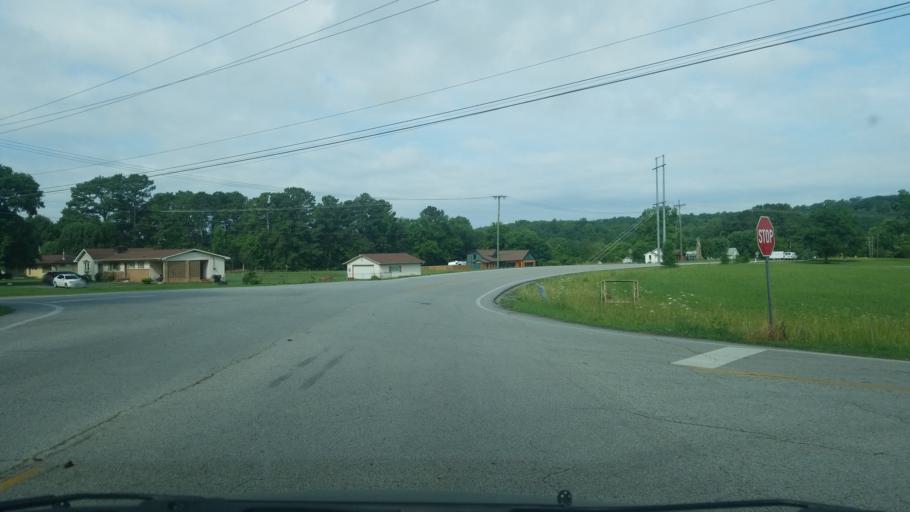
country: US
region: Tennessee
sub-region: Hamilton County
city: Apison
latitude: 35.0162
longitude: -85.0275
